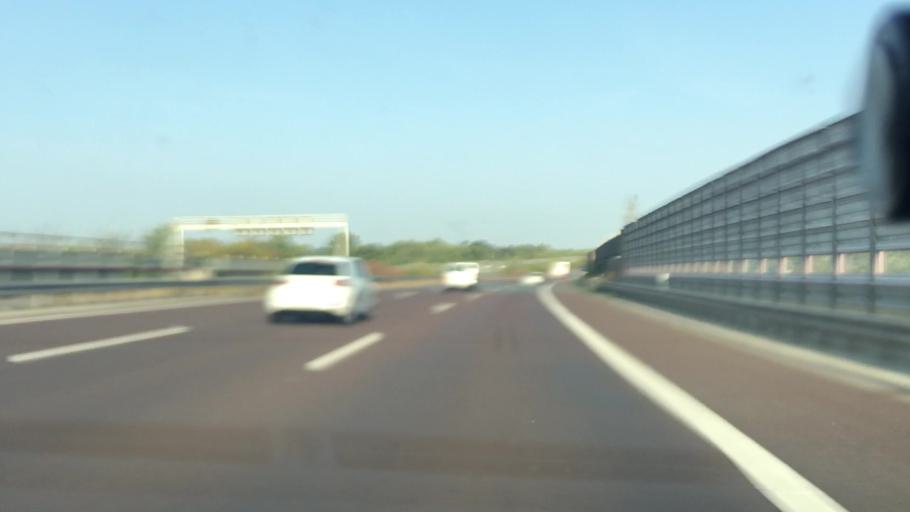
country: DE
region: Lower Saxony
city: Mariental
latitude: 52.2702
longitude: 10.9562
